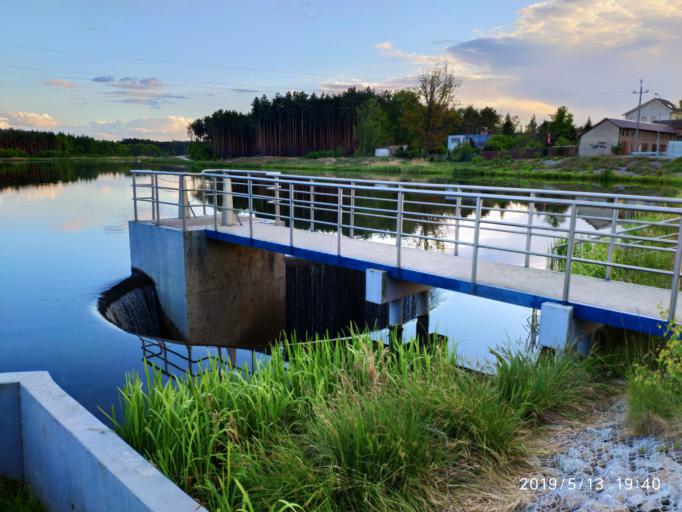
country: PL
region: Lubusz
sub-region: Powiat zielonogorski
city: Czerwiensk
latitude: 52.0069
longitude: 15.4245
